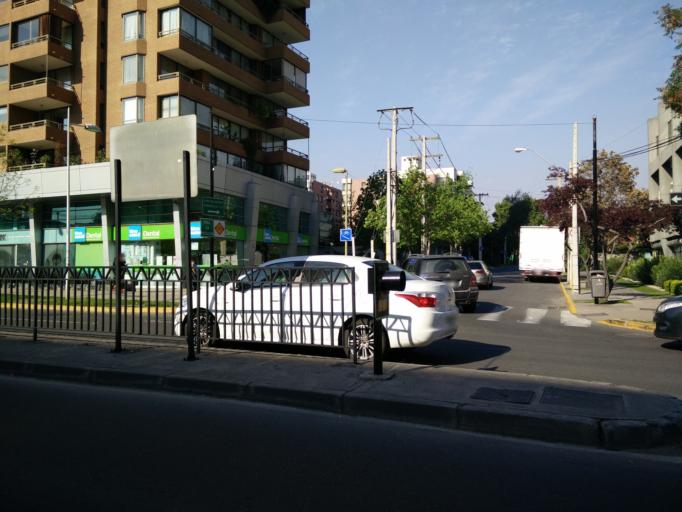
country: CL
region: Santiago Metropolitan
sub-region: Provincia de Santiago
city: Villa Presidente Frei, Nunoa, Santiago, Chile
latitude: -33.4113
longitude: -70.5663
